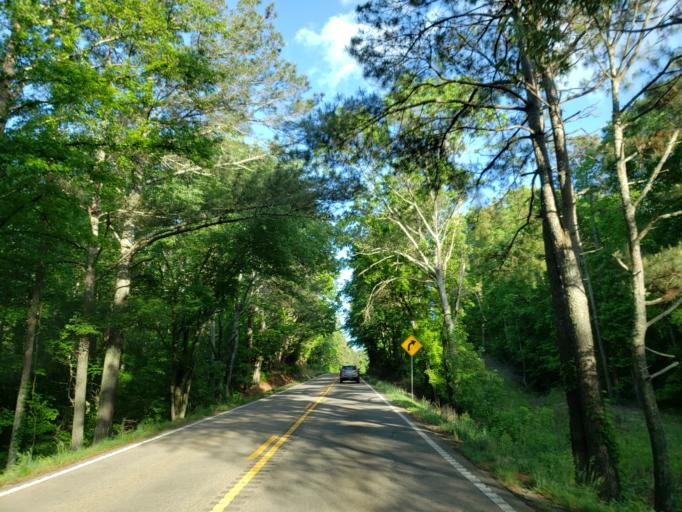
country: US
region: Georgia
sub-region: Cherokee County
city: Canton
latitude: 34.3375
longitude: -84.5693
